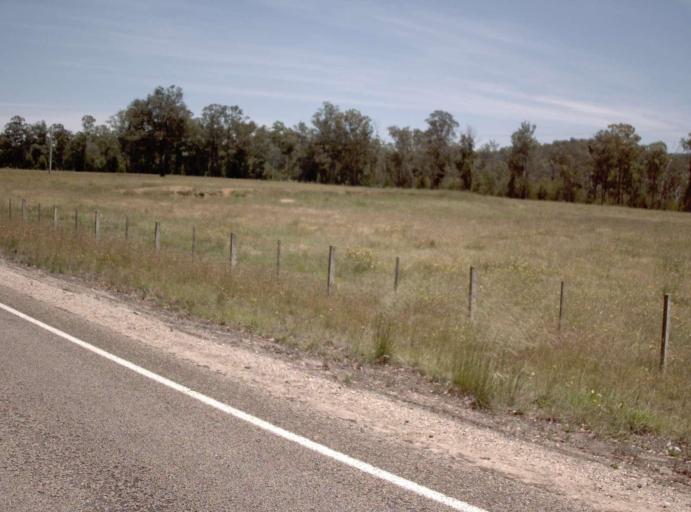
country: AU
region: Victoria
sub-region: East Gippsland
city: Lakes Entrance
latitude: -37.6784
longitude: 147.8498
